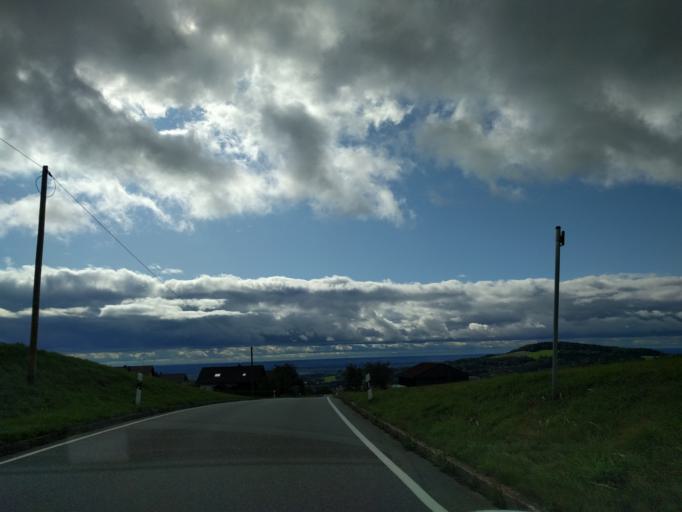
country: DE
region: Bavaria
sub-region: Lower Bavaria
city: Schaufling
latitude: 48.8259
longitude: 13.0551
